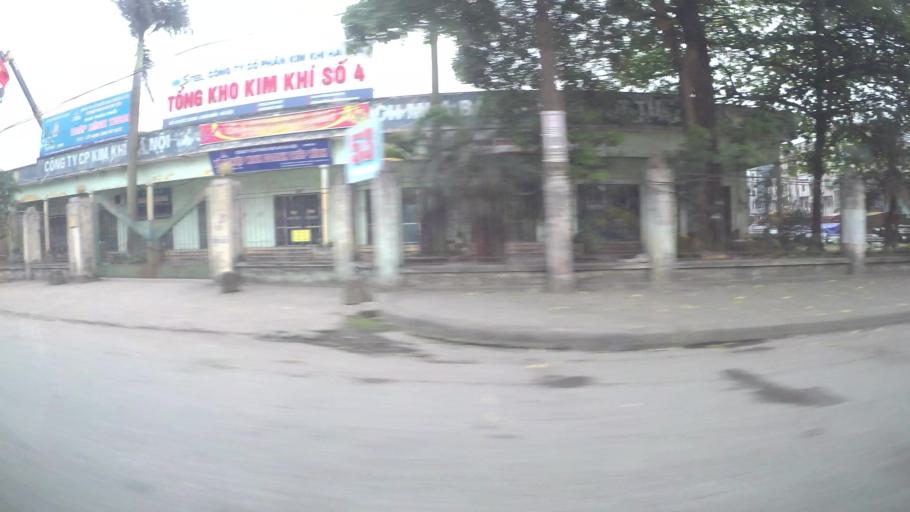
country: VN
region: Ha Noi
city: Hoan Kiem
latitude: 21.0662
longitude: 105.8922
